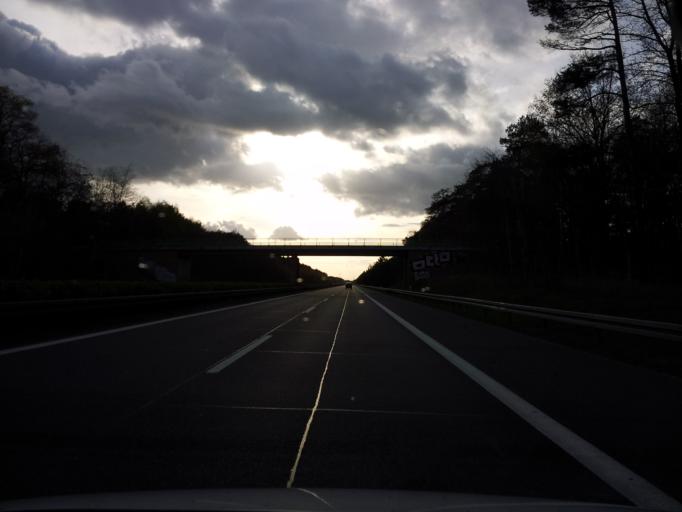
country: DE
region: Brandenburg
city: Kolkwitz
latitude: 51.7258
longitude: 14.2276
